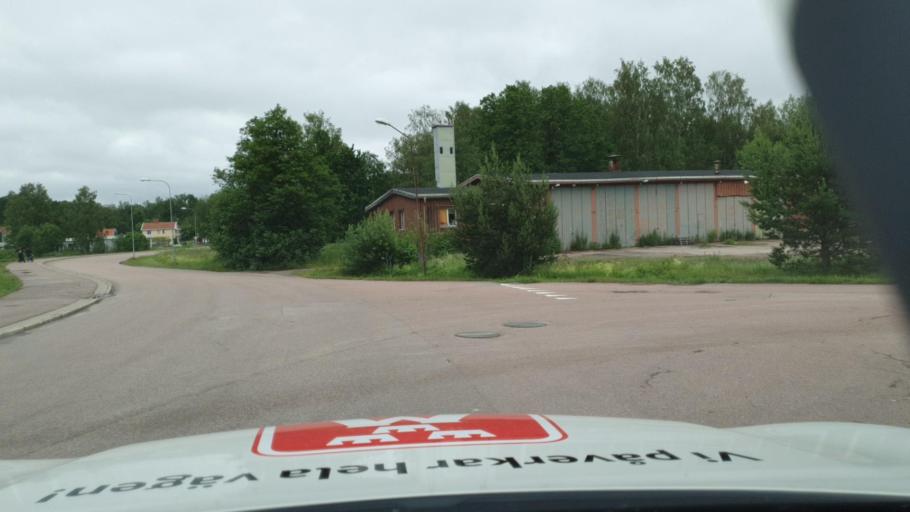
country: SE
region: Vaermland
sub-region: Grums Kommun
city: Grums
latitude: 59.3622
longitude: 13.1097
